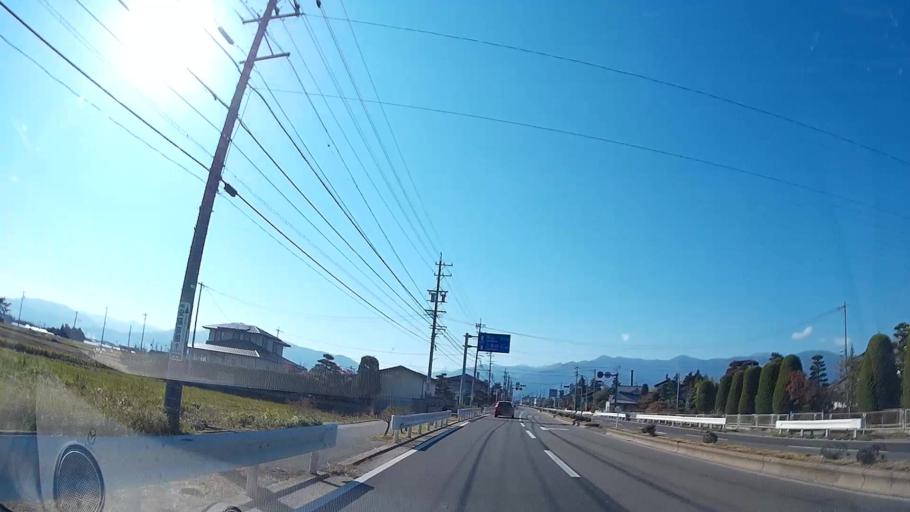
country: JP
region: Nagano
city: Matsumoto
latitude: 36.2275
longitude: 137.9304
